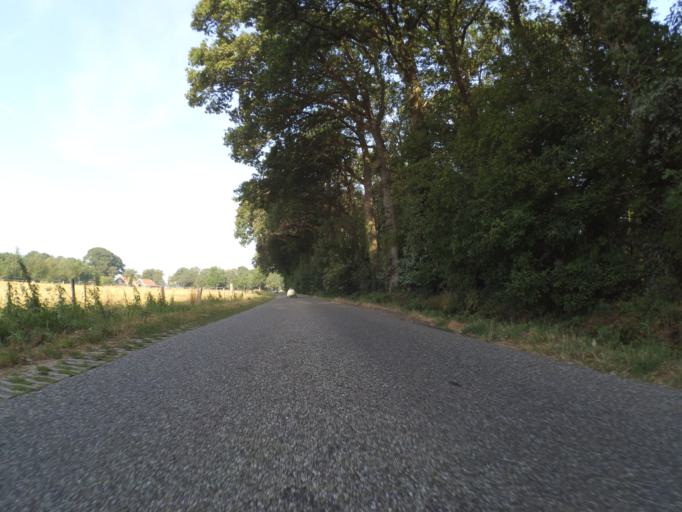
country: NL
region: Overijssel
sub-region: Gemeente Tubbergen
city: Tubbergen
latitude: 52.3598
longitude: 6.8411
